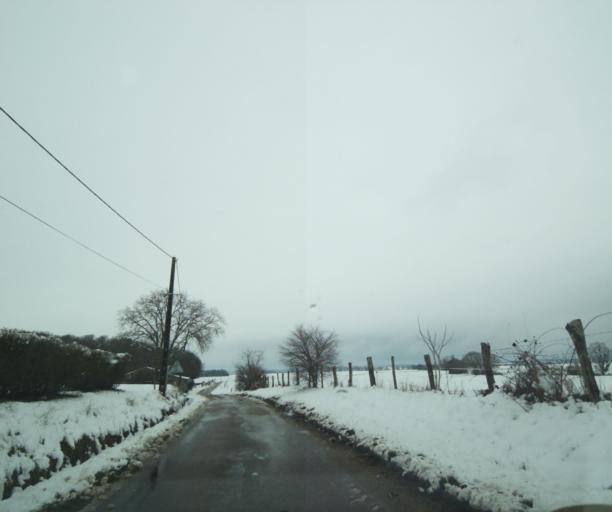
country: FR
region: Champagne-Ardenne
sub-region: Departement de la Haute-Marne
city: Montier-en-Der
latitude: 48.4251
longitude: 4.7891
